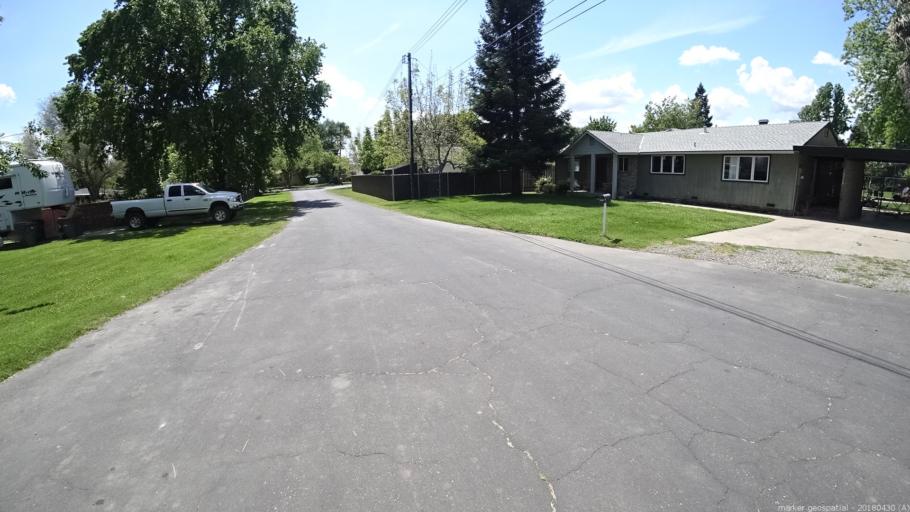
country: US
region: California
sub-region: Yolo County
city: West Sacramento
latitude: 38.5402
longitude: -121.5239
